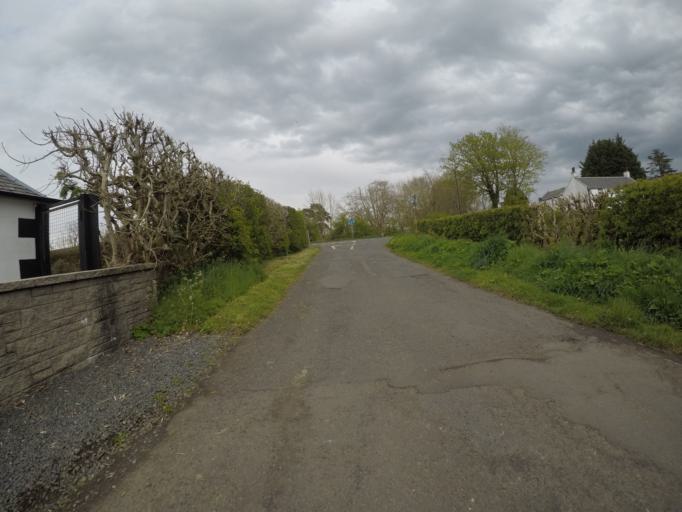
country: GB
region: Scotland
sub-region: East Ayrshire
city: Kilmarnock
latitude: 55.6564
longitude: -4.4459
